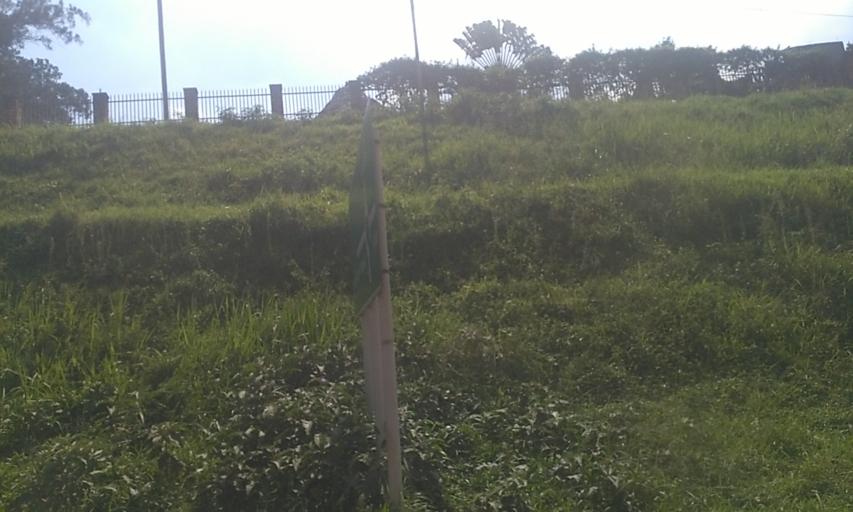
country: UG
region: Central Region
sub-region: Wakiso District
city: Kireka
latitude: 0.3643
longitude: 32.6057
